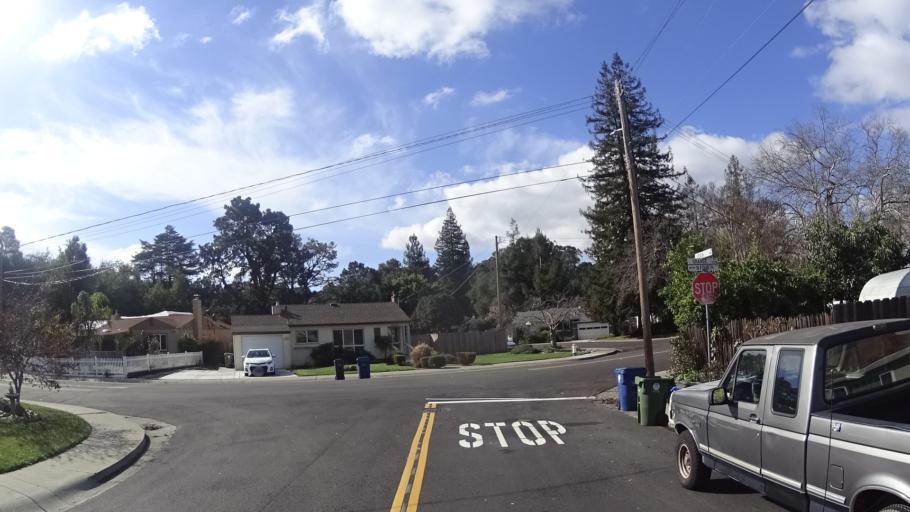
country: US
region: California
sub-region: Alameda County
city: Castro Valley
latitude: 37.6831
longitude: -122.0784
